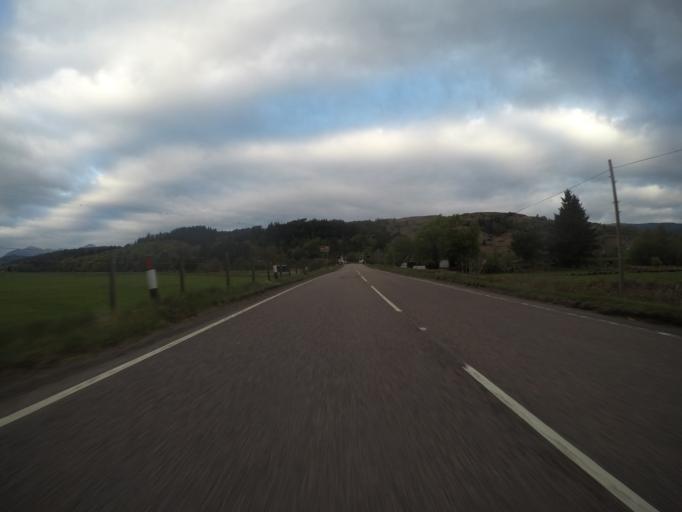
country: GB
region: Scotland
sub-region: Highland
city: Spean Bridge
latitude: 57.0924
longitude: -4.7416
